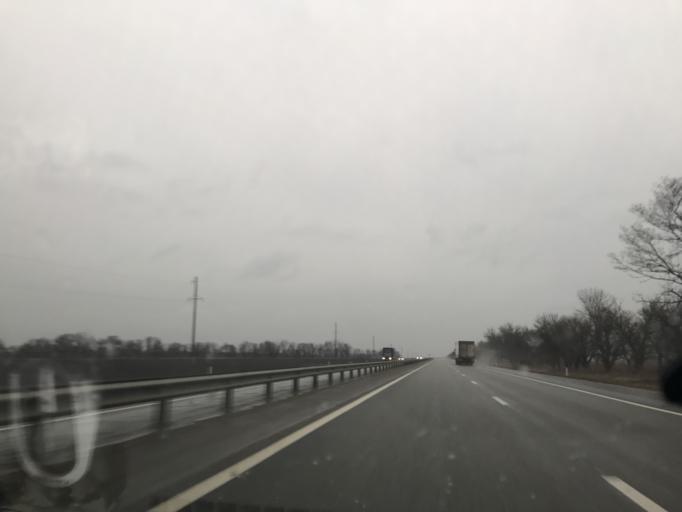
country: RU
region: Krasnodarskiy
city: Kislyakovskaya
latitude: 46.3936
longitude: 39.7351
